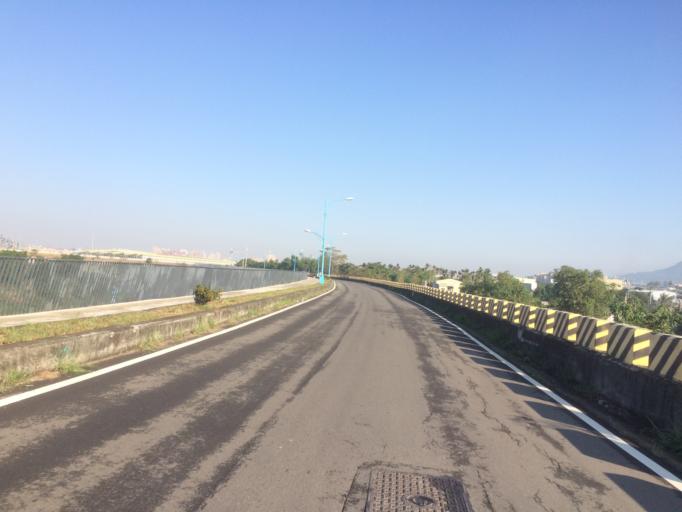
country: TW
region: Taiwan
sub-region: Taichung City
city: Taichung
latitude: 24.1837
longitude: 120.7120
